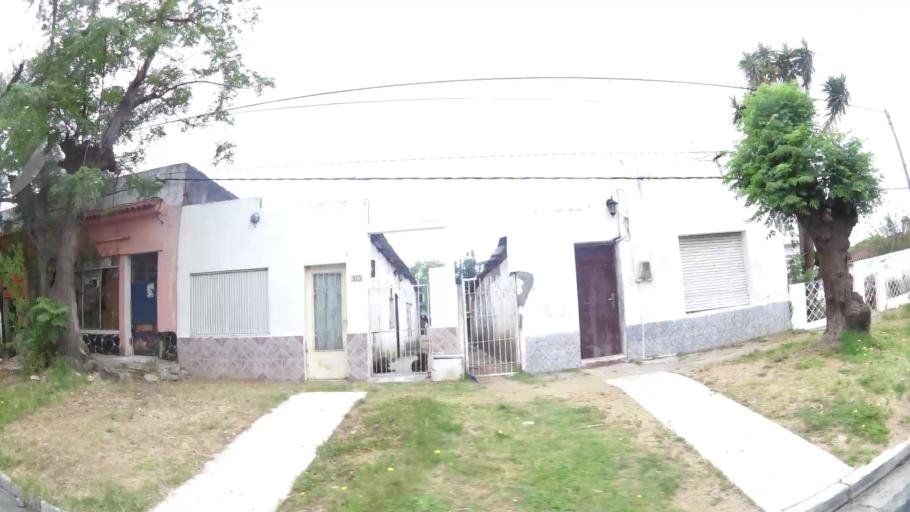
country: UY
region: Canelones
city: Las Piedras
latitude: -34.7302
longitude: -56.2110
